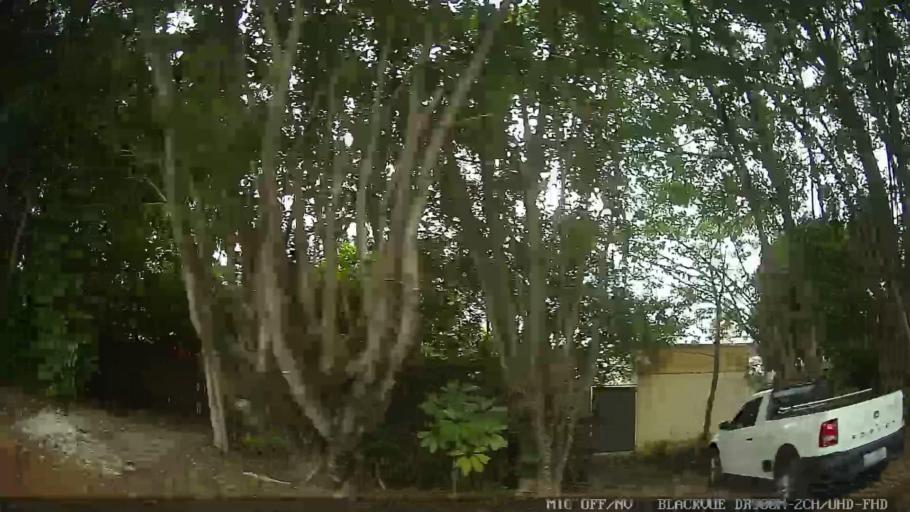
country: BR
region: Sao Paulo
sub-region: Atibaia
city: Atibaia
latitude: -23.1260
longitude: -46.5551
